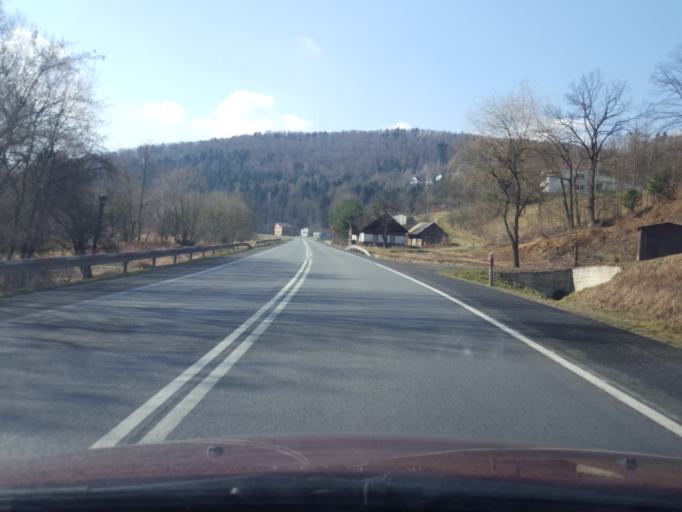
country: PL
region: Lesser Poland Voivodeship
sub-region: Powiat nowosadecki
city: Lososina Dolna
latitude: 49.7824
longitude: 20.6443
